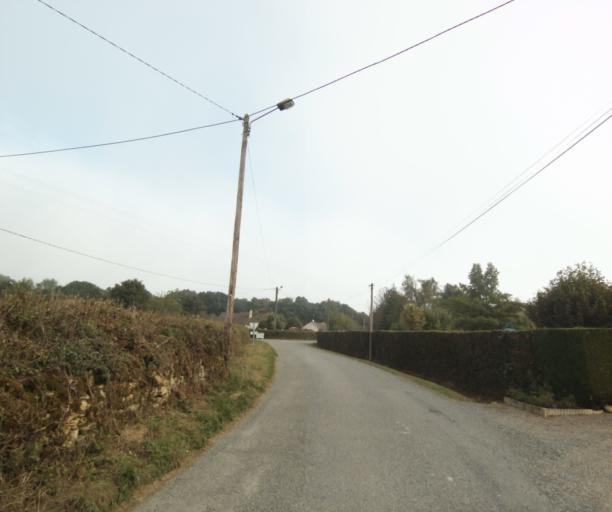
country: FR
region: Bourgogne
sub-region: Departement de Saone-et-Loire
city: Charolles
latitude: 46.4386
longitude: 4.2627
